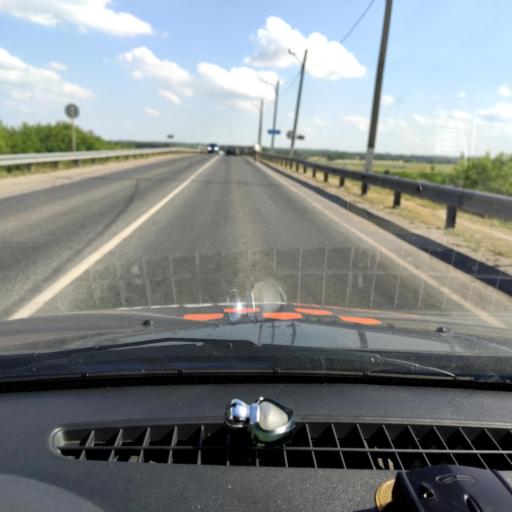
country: RU
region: Lipetsk
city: Yelets
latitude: 52.5873
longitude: 38.5089
